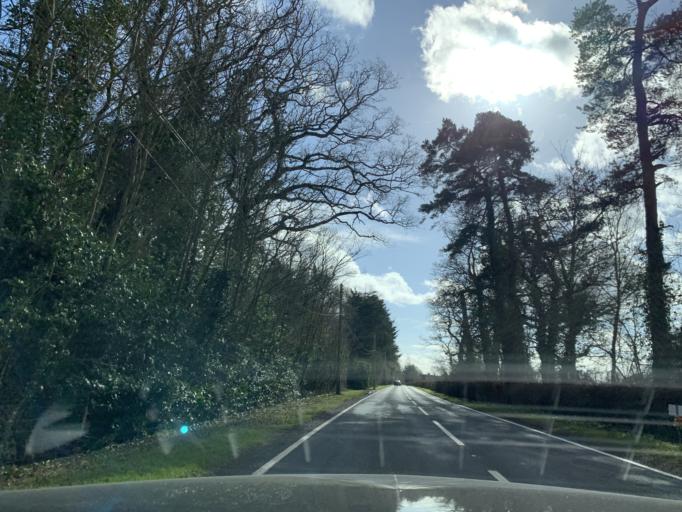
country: GB
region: England
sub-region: West Sussex
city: Crawley Down
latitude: 51.0820
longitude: -0.0782
